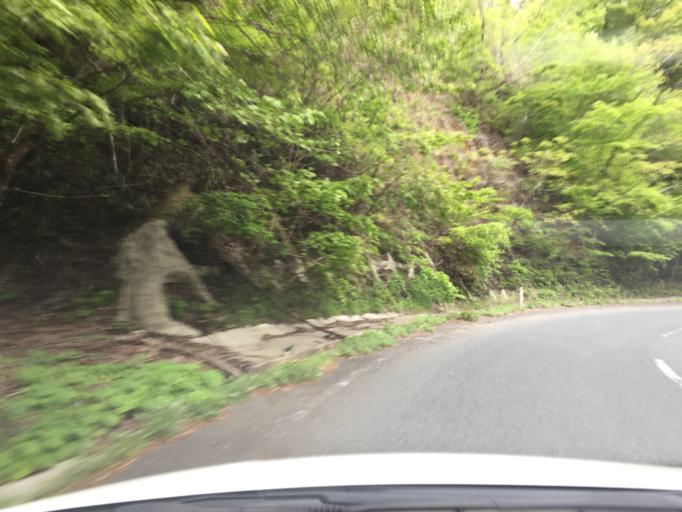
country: JP
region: Miyagi
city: Marumori
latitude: 37.7284
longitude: 140.8029
